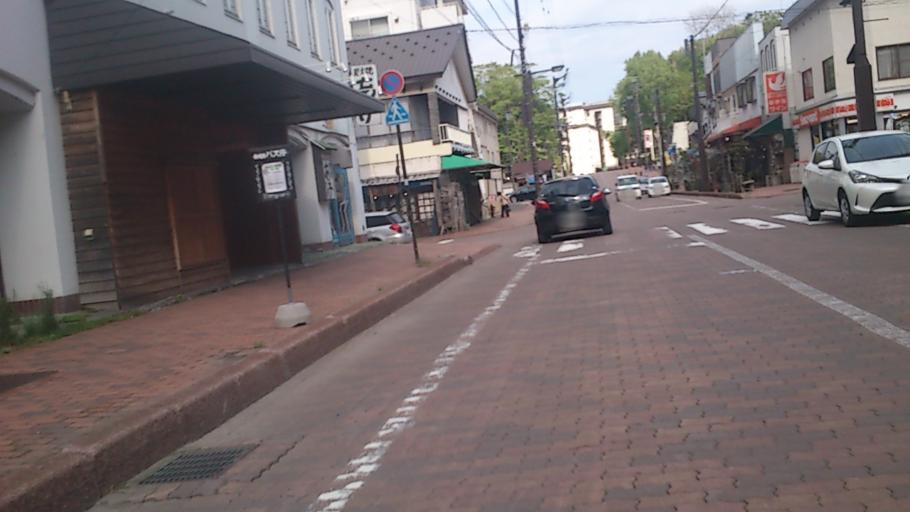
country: JP
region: Hokkaido
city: Bihoro
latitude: 43.4339
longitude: 144.0918
